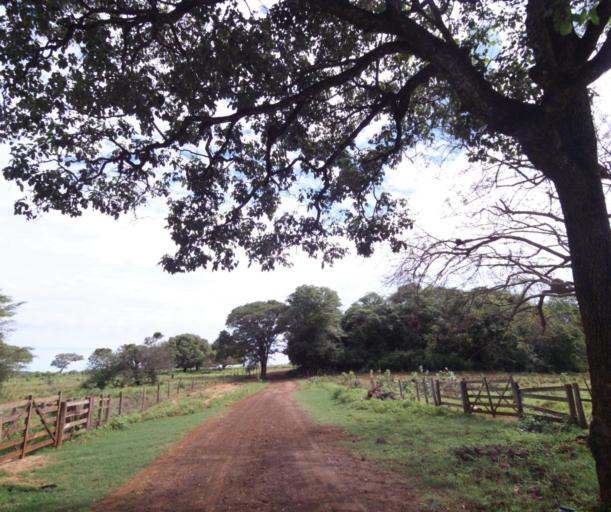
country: BR
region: Bahia
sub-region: Carinhanha
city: Carinhanha
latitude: -14.2409
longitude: -44.4129
